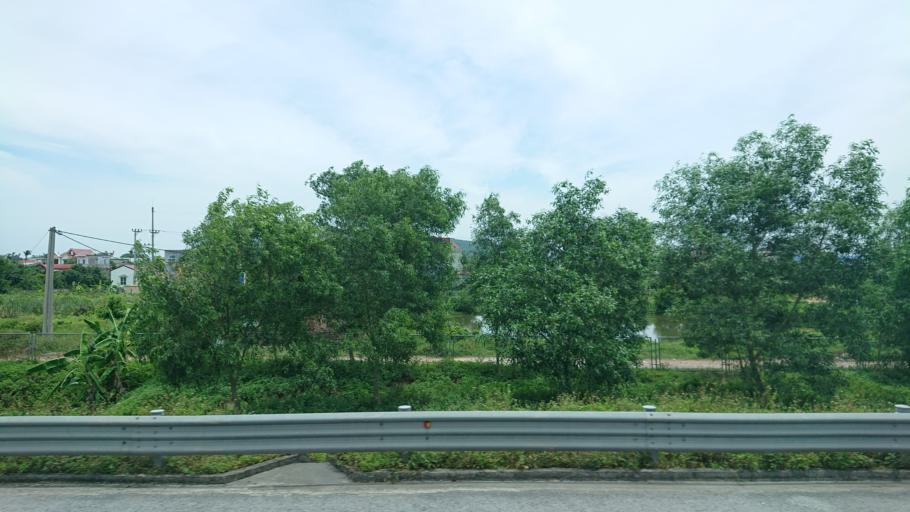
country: VN
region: Hai Phong
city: Nui Doi
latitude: 20.7707
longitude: 106.6159
